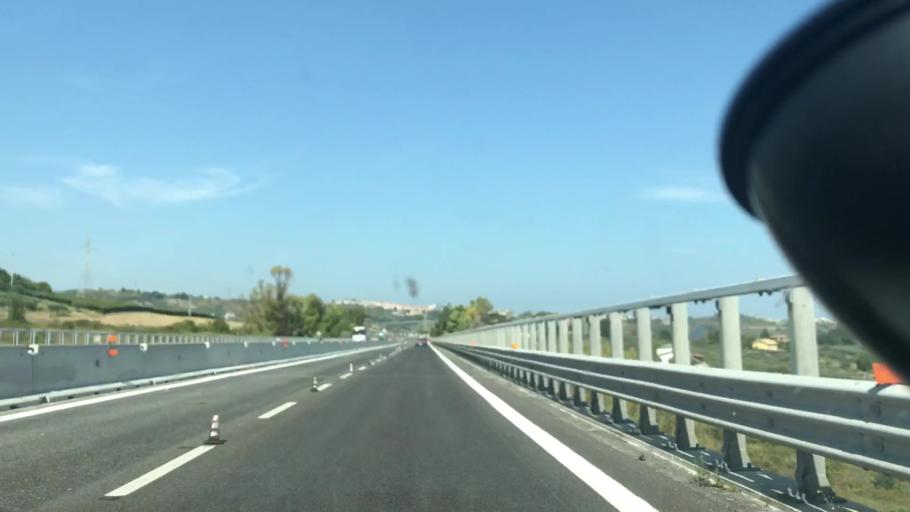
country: IT
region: Abruzzo
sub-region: Provincia di Chieti
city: Marina di Vasto
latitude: 42.0751
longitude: 14.7132
